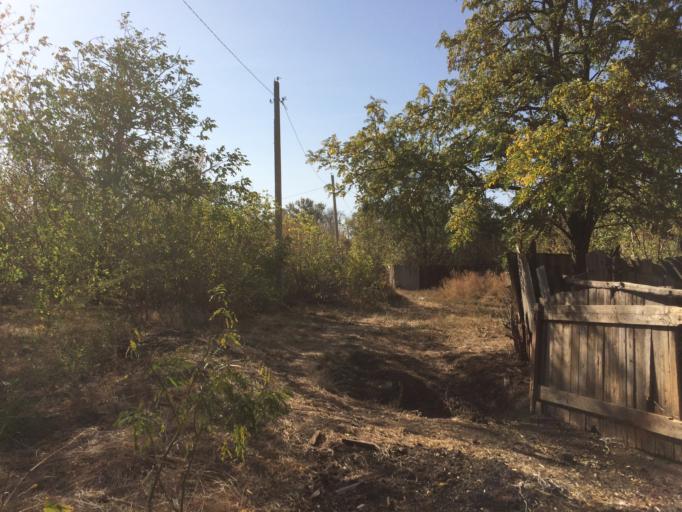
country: RU
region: Rostov
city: Tselina
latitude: 46.5140
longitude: 41.1852
